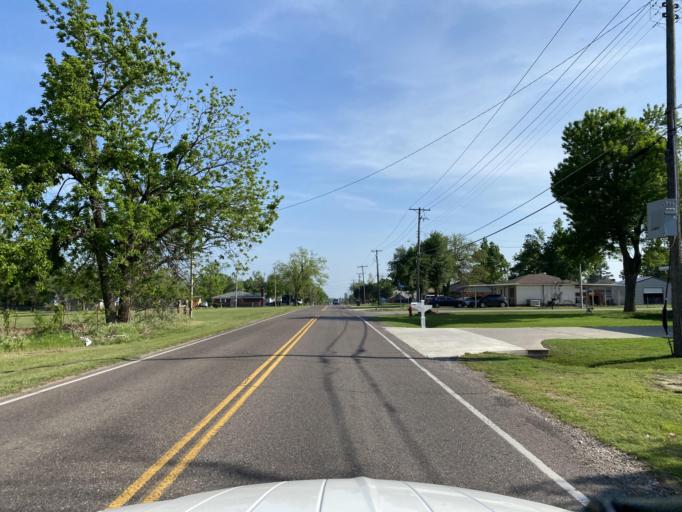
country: US
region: Oklahoma
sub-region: Oklahoma County
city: Nicoma Park
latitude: 35.4876
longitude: -97.3357
